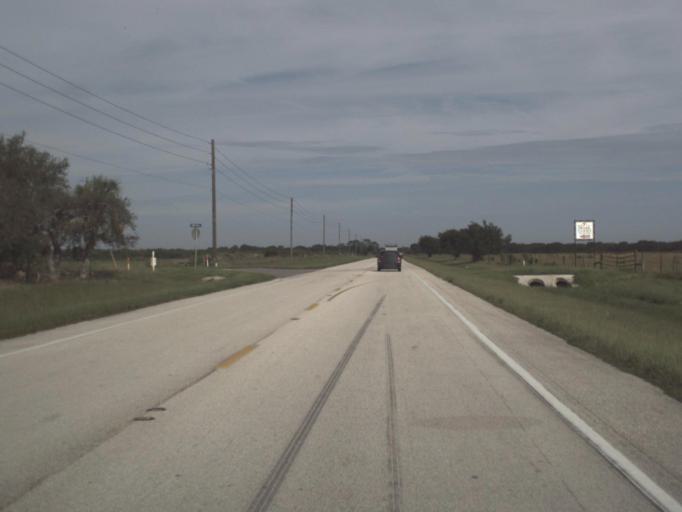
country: US
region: Florida
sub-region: DeSoto County
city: Nocatee
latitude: 27.0407
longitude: -81.7765
